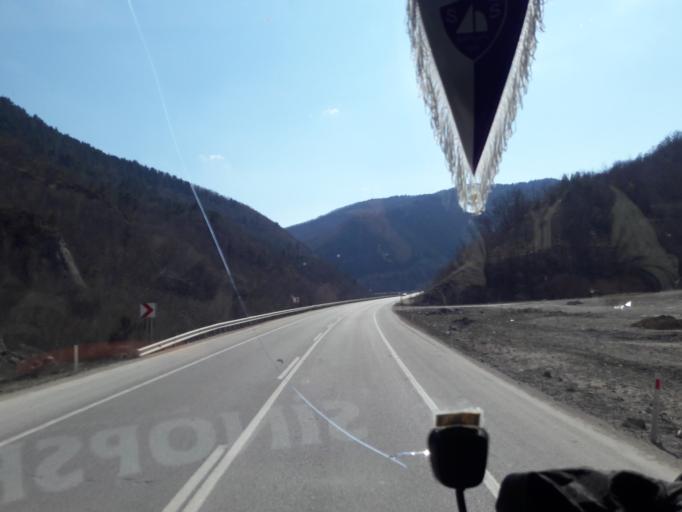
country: TR
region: Sinop
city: Erfelek
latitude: 41.7005
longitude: 34.9145
